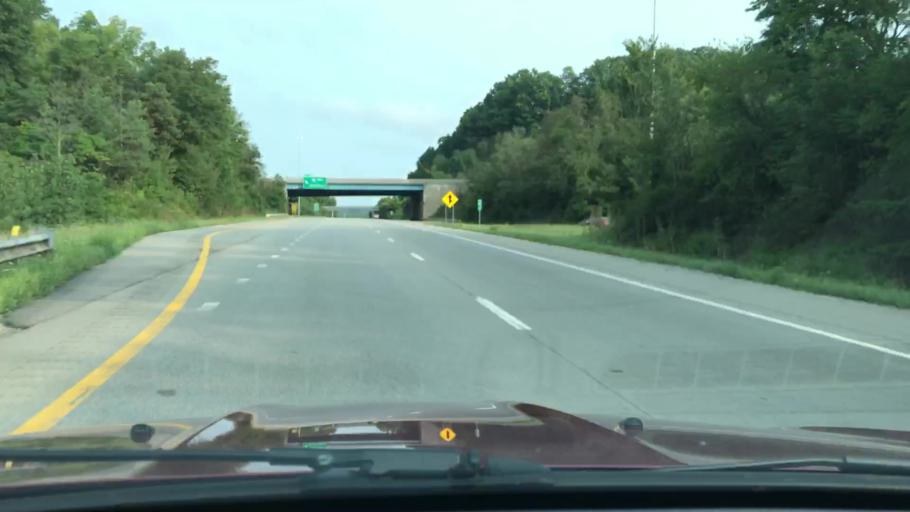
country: US
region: Ohio
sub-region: Guernsey County
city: Byesville
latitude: 39.9970
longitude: -81.5545
